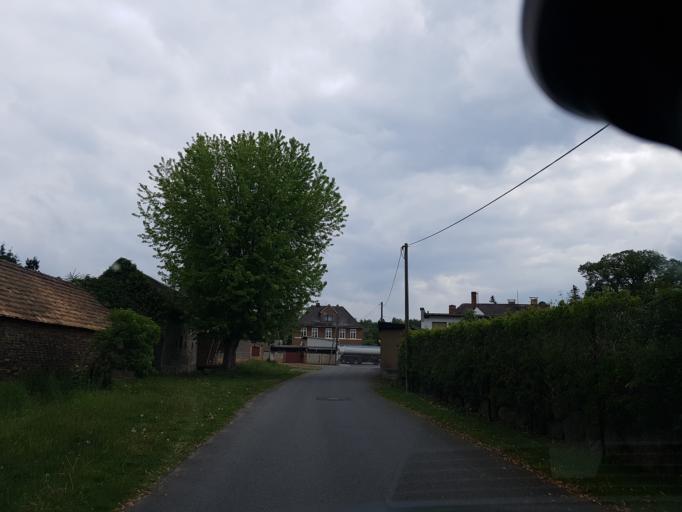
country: DE
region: Brandenburg
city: Crinitz
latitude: 51.7391
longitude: 13.7640
